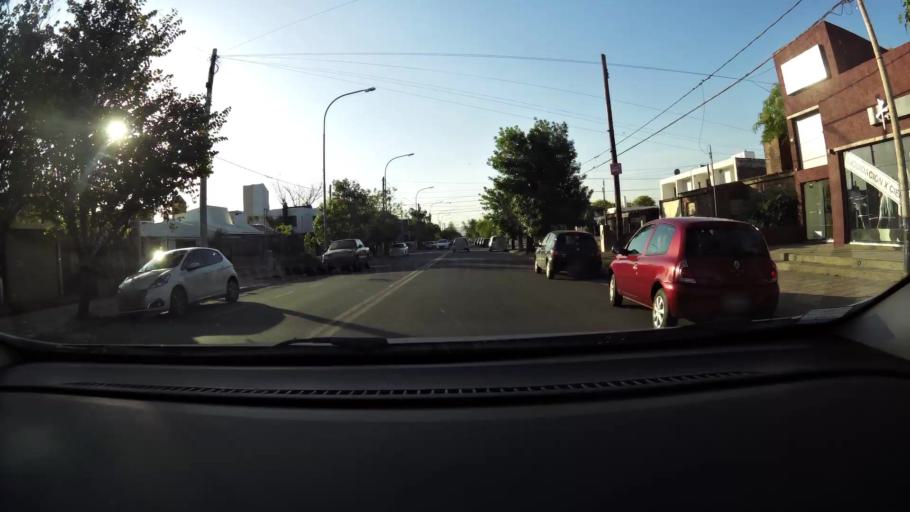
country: AR
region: Cordoba
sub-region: Departamento de Capital
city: Cordoba
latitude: -31.3850
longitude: -64.2332
